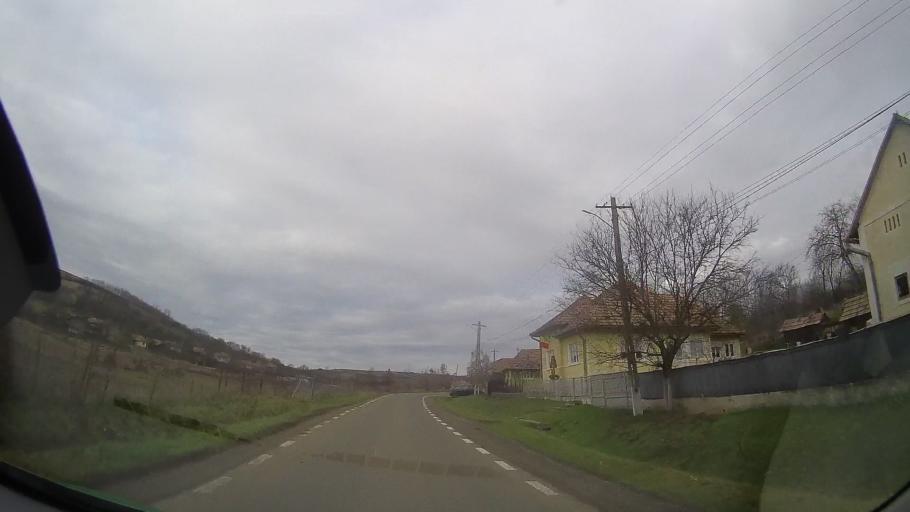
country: RO
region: Mures
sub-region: Comuna Cozma
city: Cozma
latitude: 46.8050
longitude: 24.5267
